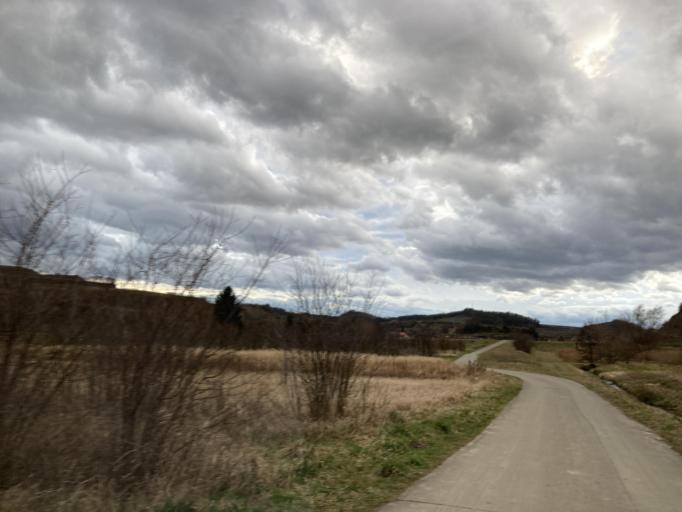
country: DE
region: Baden-Wuerttemberg
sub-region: Freiburg Region
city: Vogtsburg
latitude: 48.0930
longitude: 7.6462
